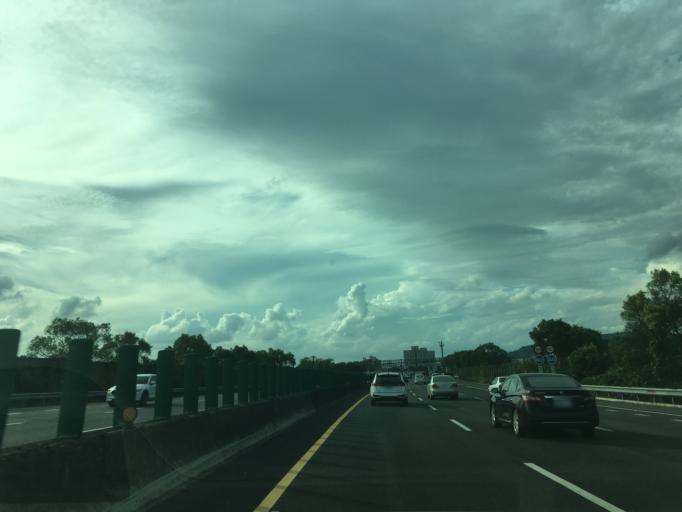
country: TW
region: Taiwan
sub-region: Nantou
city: Nantou
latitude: 23.9040
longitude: 120.7042
